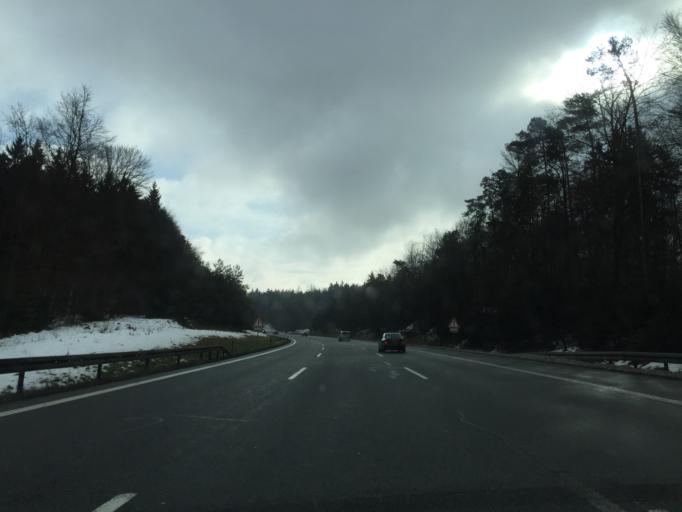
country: DE
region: Bavaria
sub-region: Upper Bavaria
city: Denkendorf
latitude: 48.9694
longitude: 11.4020
